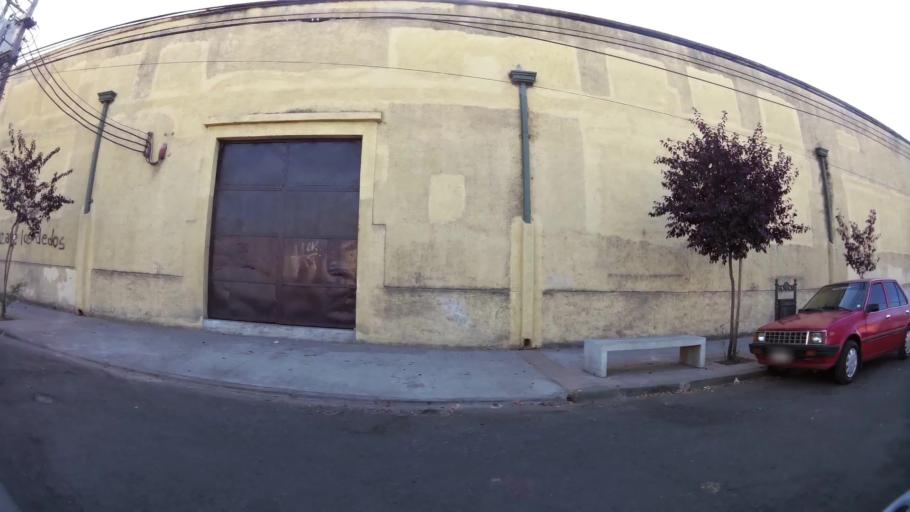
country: CL
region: Maule
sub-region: Provincia de Talca
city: Talca
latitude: -35.4332
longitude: -71.6541
